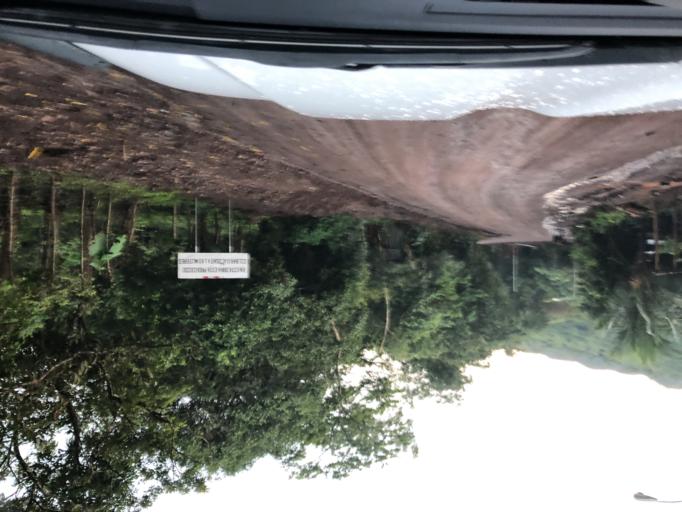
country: NI
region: Chontales
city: La Libertad
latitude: 12.1789
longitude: -85.1715
